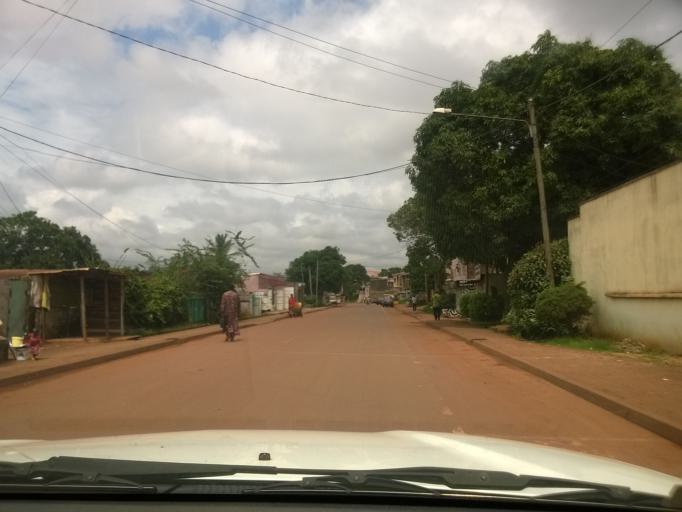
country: CM
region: Centre
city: Yaounde
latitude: 3.8686
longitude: 11.5364
